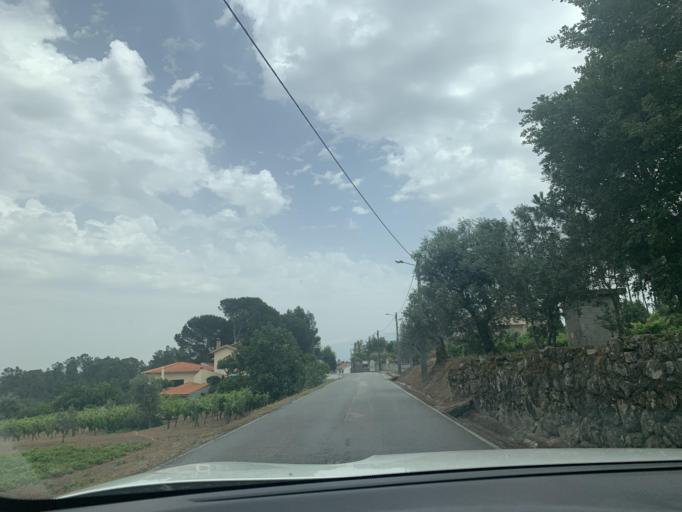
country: PT
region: Viseu
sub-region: Mangualde
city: Mangualde
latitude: 40.5620
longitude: -7.6963
